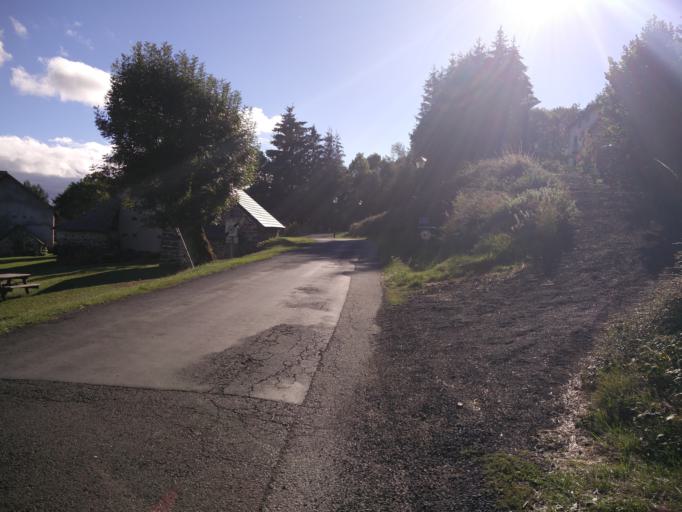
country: FR
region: Auvergne
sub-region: Departement du Puy-de-Dome
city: Gelles
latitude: 45.7250
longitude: 2.8247
